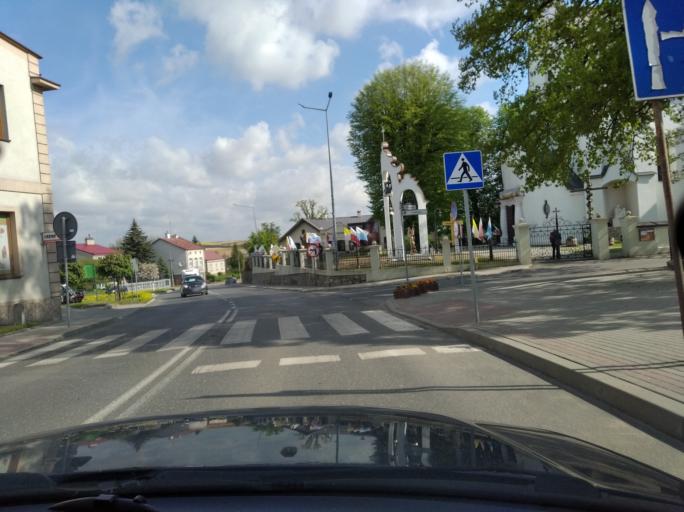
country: PL
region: Subcarpathian Voivodeship
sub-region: Powiat przeworski
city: Kanczuga
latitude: 49.9843
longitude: 22.4119
